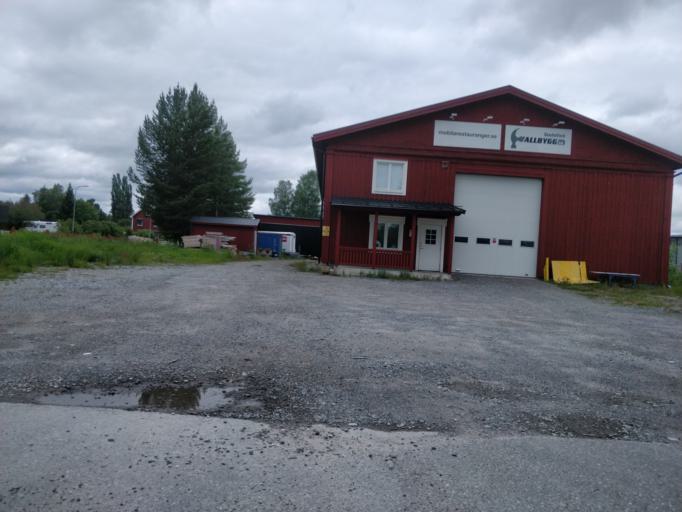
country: SE
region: Vaesterbotten
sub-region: Skelleftea Kommun
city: Viken
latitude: 64.7584
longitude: 20.8900
